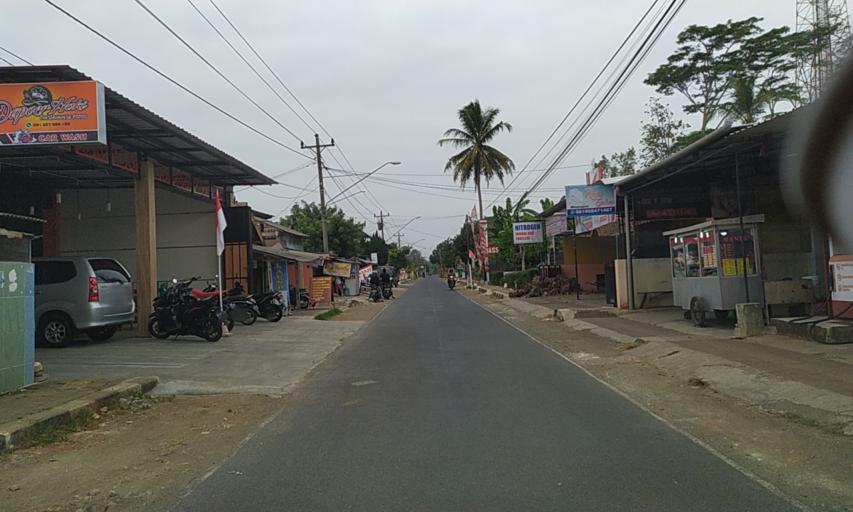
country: ID
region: Central Java
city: Kroya
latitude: -7.6684
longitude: 109.2675
